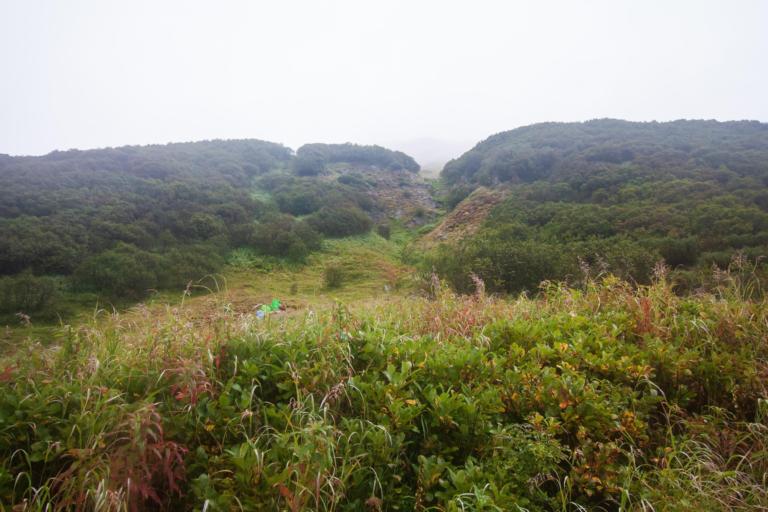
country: RU
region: Kamtsjatka
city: Yelizovo
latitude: 53.9535
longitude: 158.0658
